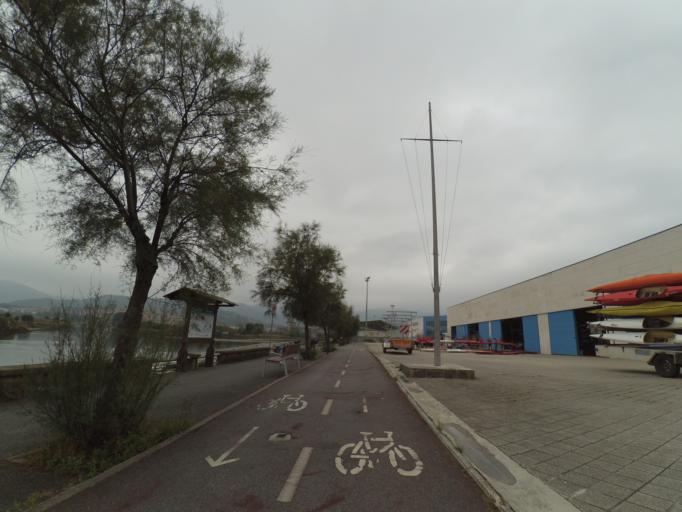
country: ES
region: Basque Country
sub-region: Provincia de Guipuzcoa
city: Irun
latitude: 43.3470
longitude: -1.7856
